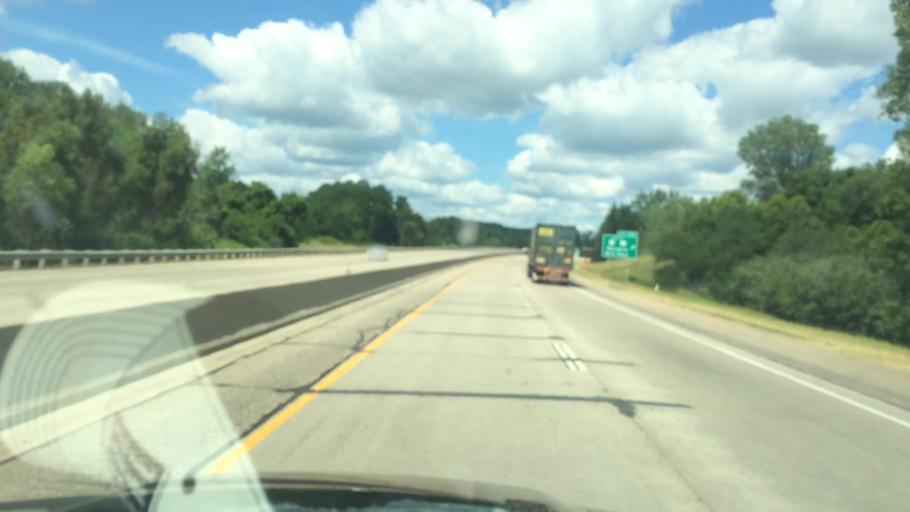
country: US
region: Wisconsin
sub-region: Waupaca County
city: Waupaca
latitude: 44.3412
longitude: -89.0897
